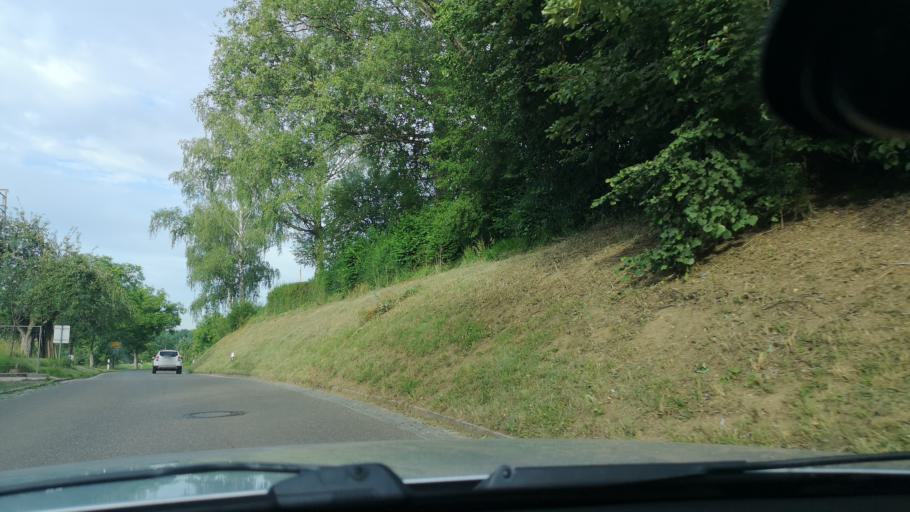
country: DE
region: Baden-Wuerttemberg
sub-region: Regierungsbezirk Stuttgart
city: Ohmden
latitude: 48.6455
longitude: 9.5180
